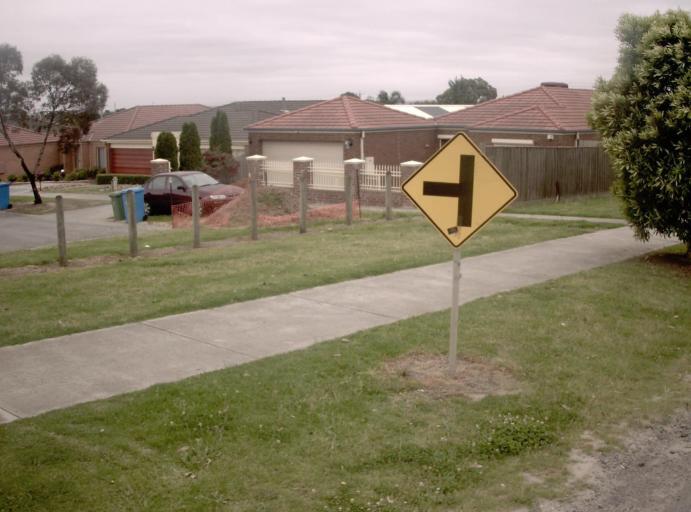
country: AU
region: Victoria
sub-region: Casey
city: Lynbrook
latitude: -38.0416
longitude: 145.2659
